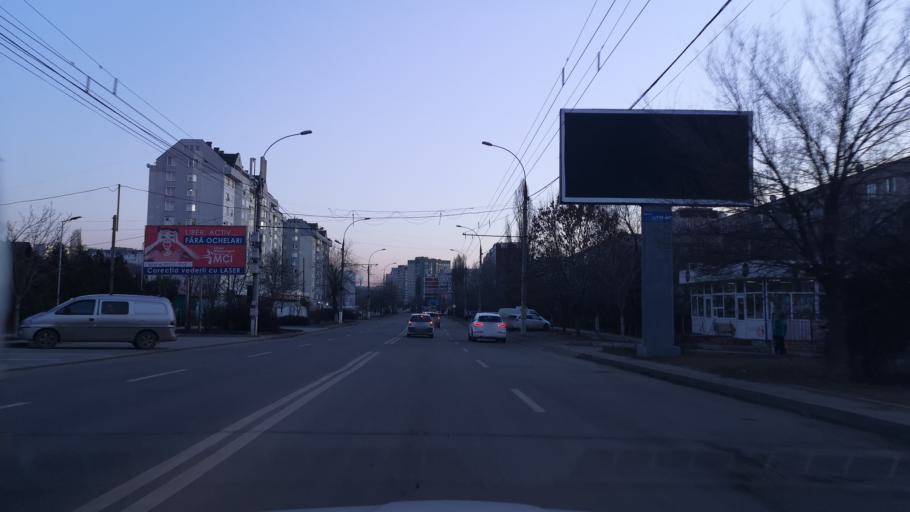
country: MD
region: Chisinau
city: Stauceni
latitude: 47.0612
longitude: 28.8462
